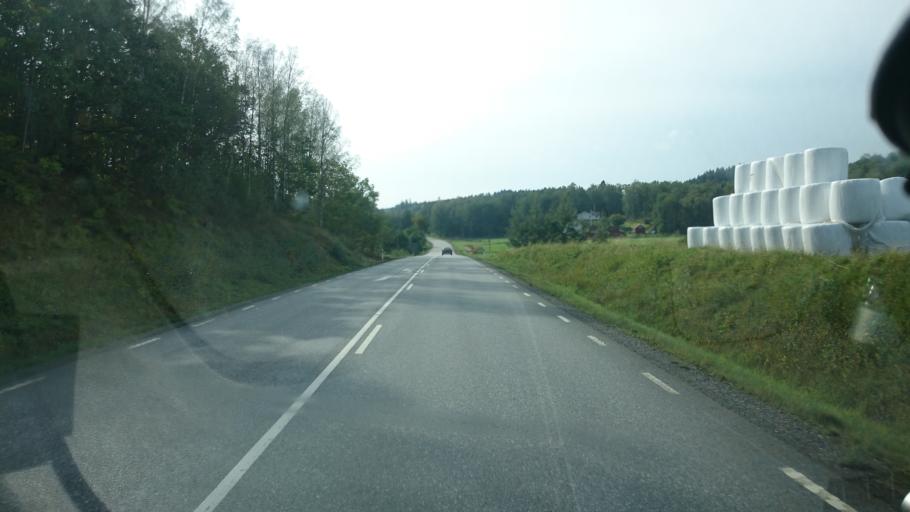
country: SE
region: Vaestra Goetaland
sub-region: Alingsas Kommun
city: Sollebrunn
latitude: 58.0468
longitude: 12.4680
